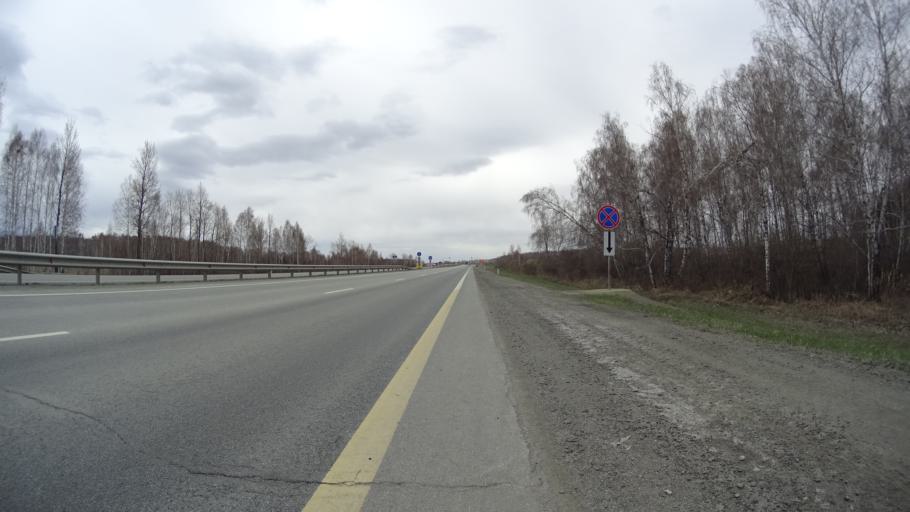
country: RU
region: Chelyabinsk
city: Yemanzhelinka
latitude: 54.8273
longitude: 61.3106
